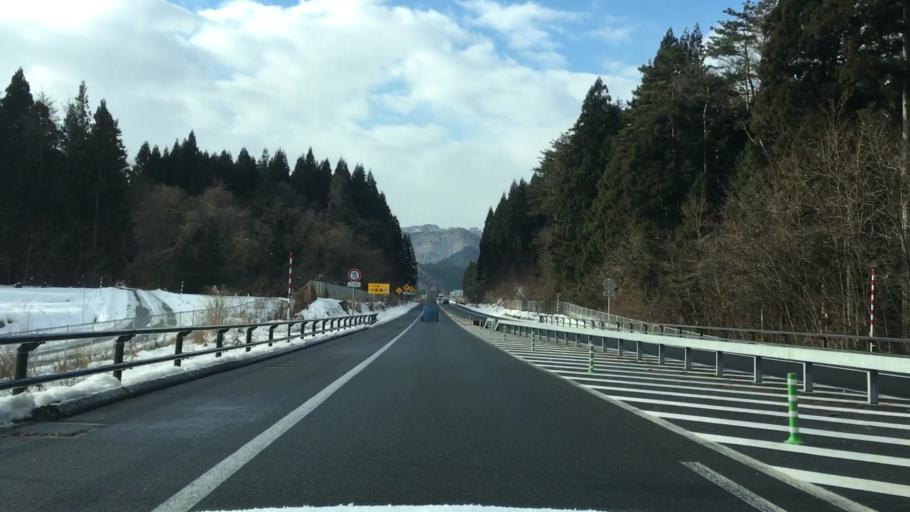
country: JP
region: Akita
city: Odate
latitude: 40.2444
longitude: 140.5100
